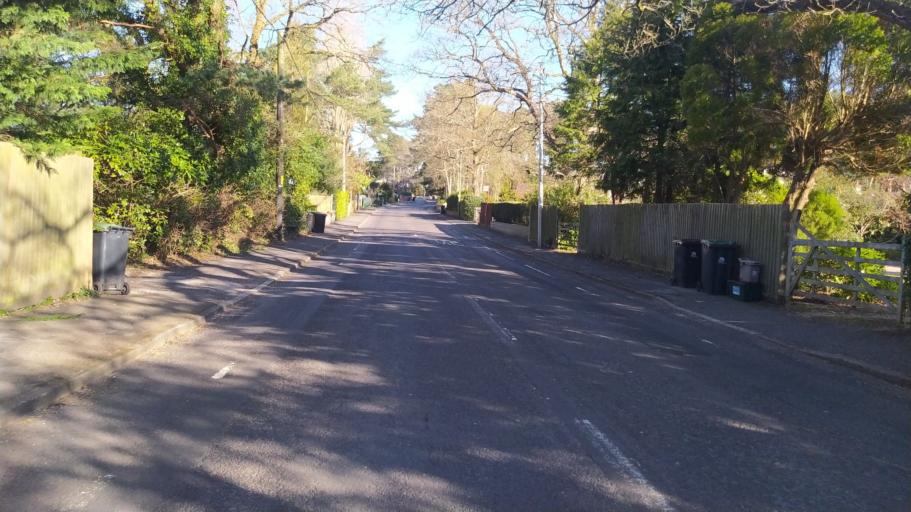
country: GB
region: England
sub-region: Dorset
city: St Leonards
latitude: 50.8340
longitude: -1.8381
